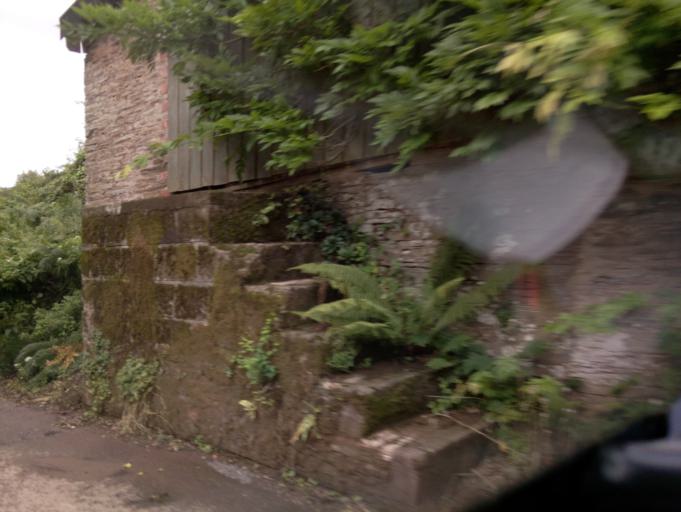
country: GB
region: England
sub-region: Devon
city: Kingsbridge
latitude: 50.2770
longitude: -3.7193
